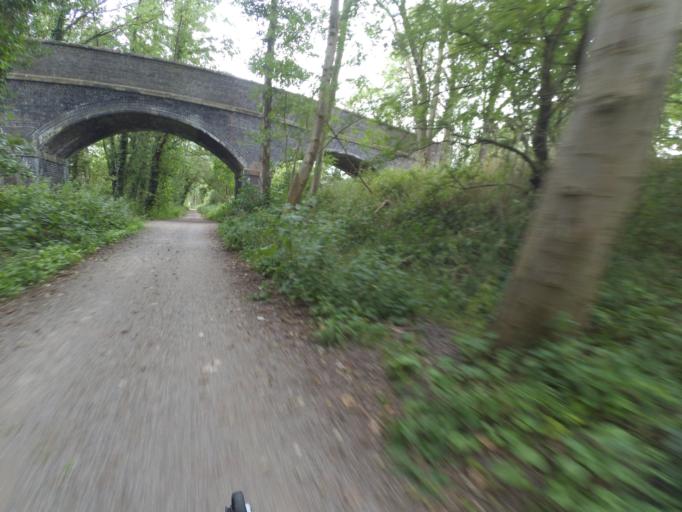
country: GB
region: England
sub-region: Staffordshire
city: Gnosall
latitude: 52.7724
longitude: -2.3022
